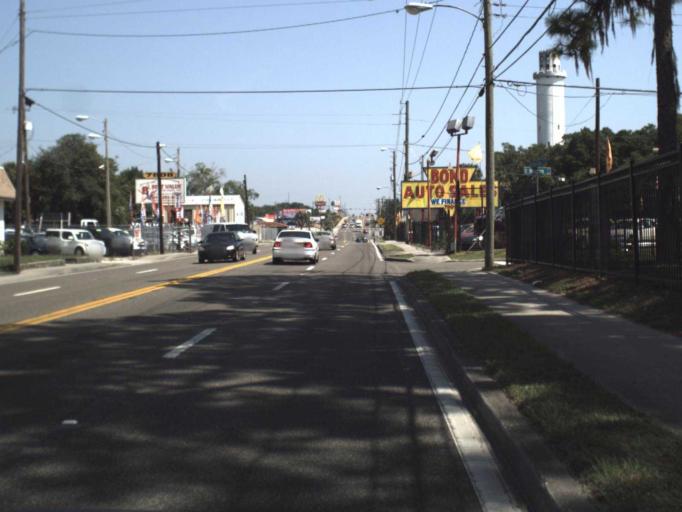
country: US
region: Florida
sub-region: Hillsborough County
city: Carrollwood
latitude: 28.0187
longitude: -82.4595
